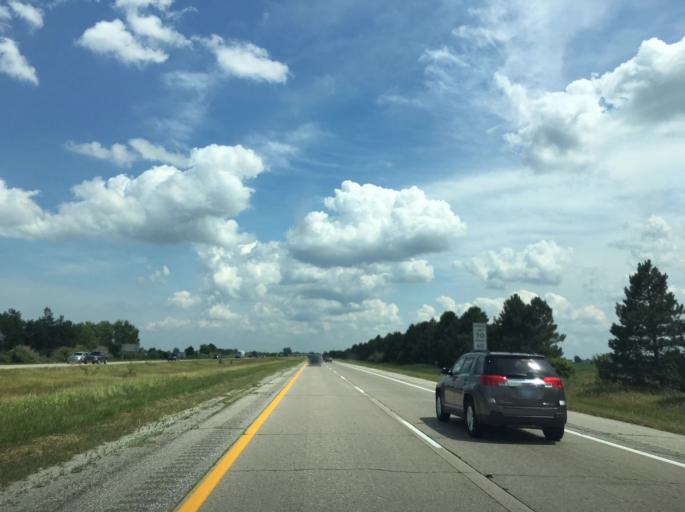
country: US
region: Michigan
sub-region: Bay County
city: Auburn
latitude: 43.6599
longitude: -84.0039
